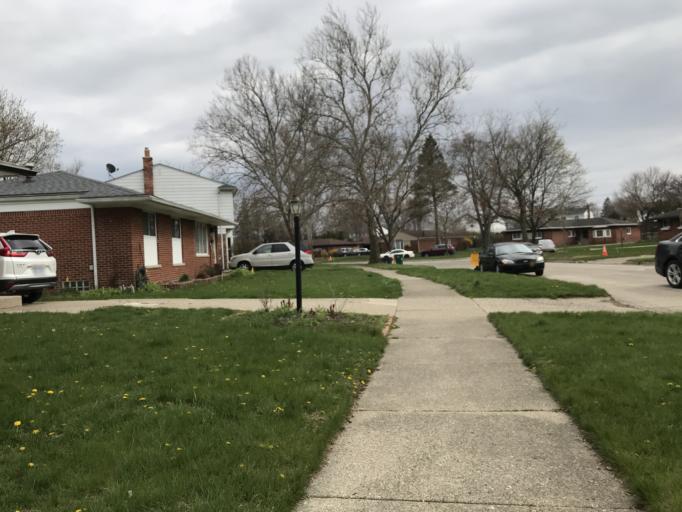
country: US
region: Michigan
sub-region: Oakland County
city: Farmington
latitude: 42.4597
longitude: -83.3469
